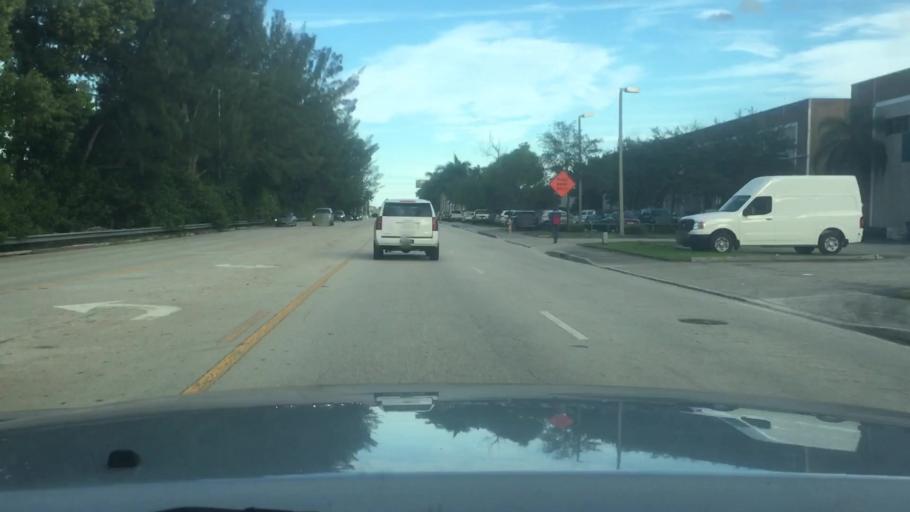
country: US
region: Florida
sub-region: Miami-Dade County
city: Fountainebleau
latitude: 25.7832
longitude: -80.3452
